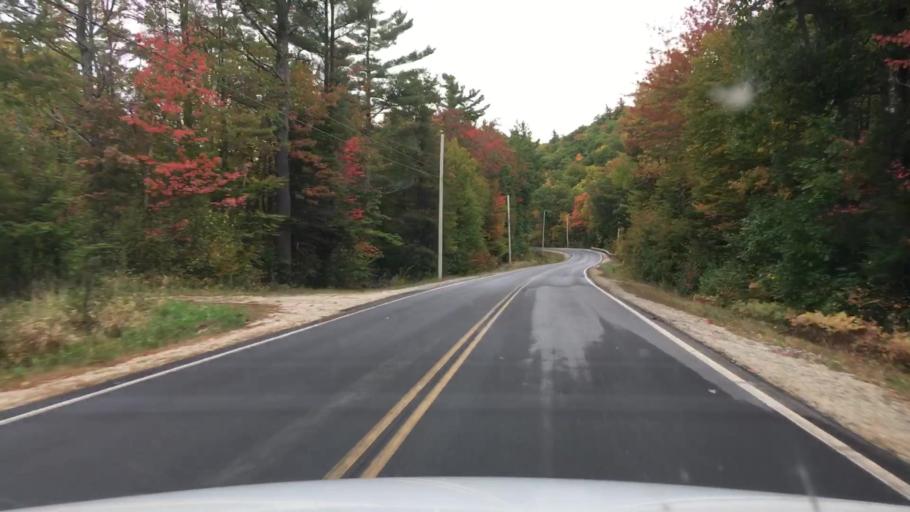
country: US
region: Maine
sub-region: Oxford County
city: Bethel
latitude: 44.2947
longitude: -70.7361
